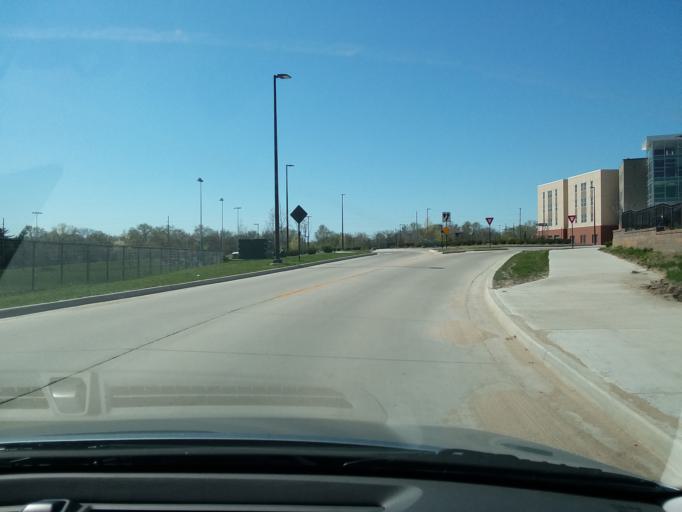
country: US
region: Kansas
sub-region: Douglas County
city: Lawrence
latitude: 38.9521
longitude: -95.2554
